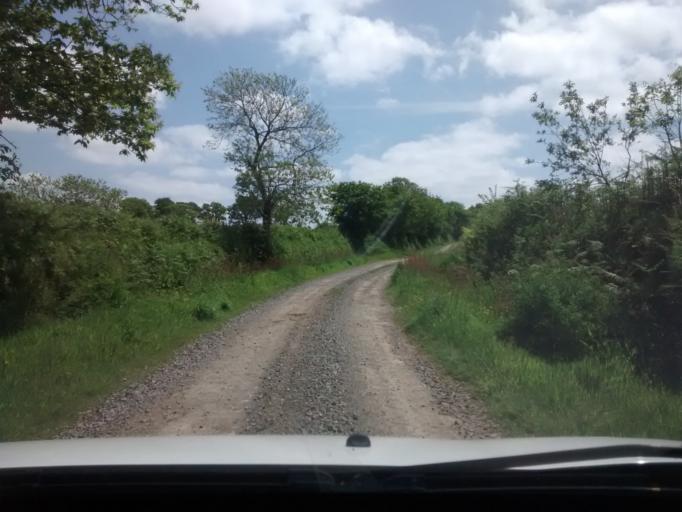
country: FR
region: Brittany
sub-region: Departement des Cotes-d'Armor
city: Louannec
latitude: 48.7843
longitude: -3.4088
